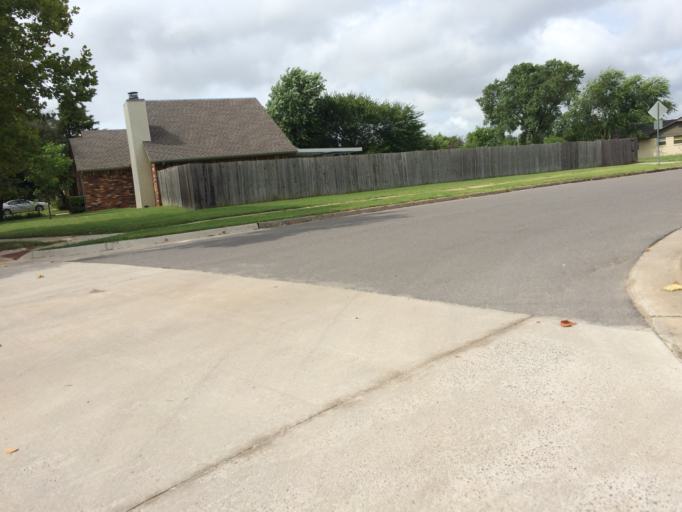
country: US
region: Oklahoma
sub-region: Cleveland County
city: Hall Park
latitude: 35.2220
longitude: -97.4163
